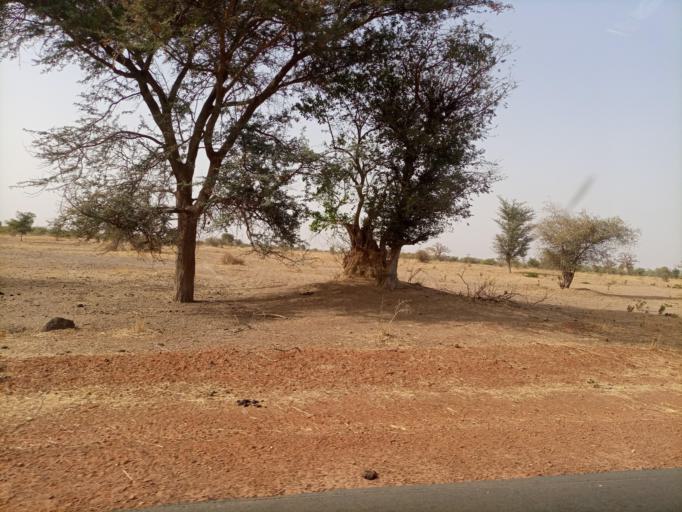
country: SN
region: Fatick
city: Foundiougne
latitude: 14.1277
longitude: -16.4132
